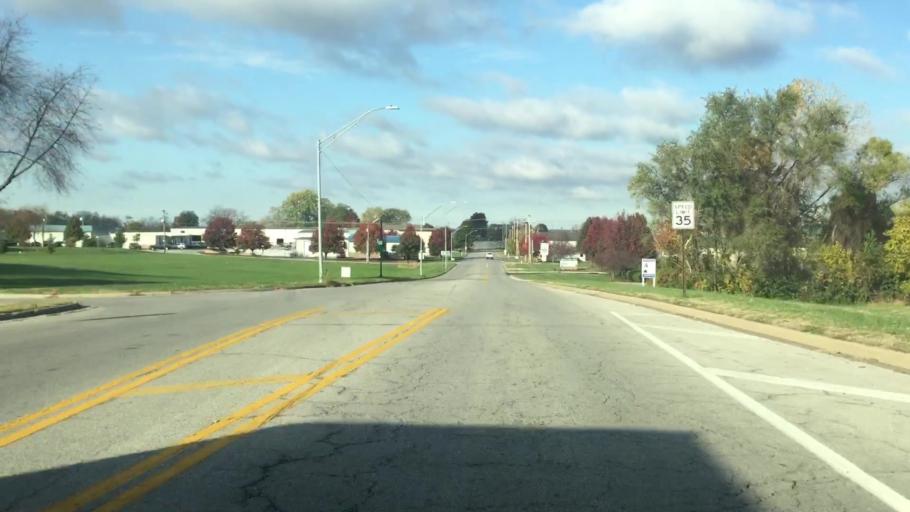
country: US
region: Missouri
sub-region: Jackson County
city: Grandview
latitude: 38.8897
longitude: -94.5409
